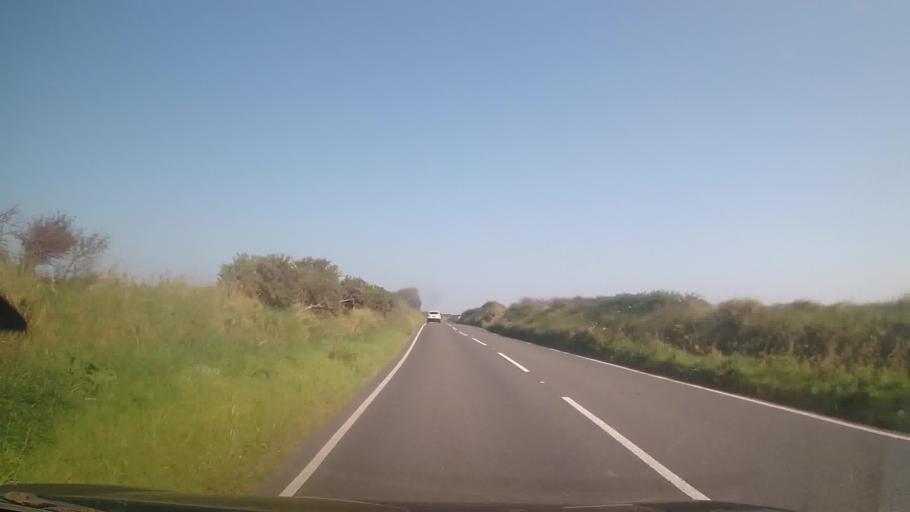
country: GB
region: Wales
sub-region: Pembrokeshire
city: Saint David's
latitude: 51.8990
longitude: -5.2189
